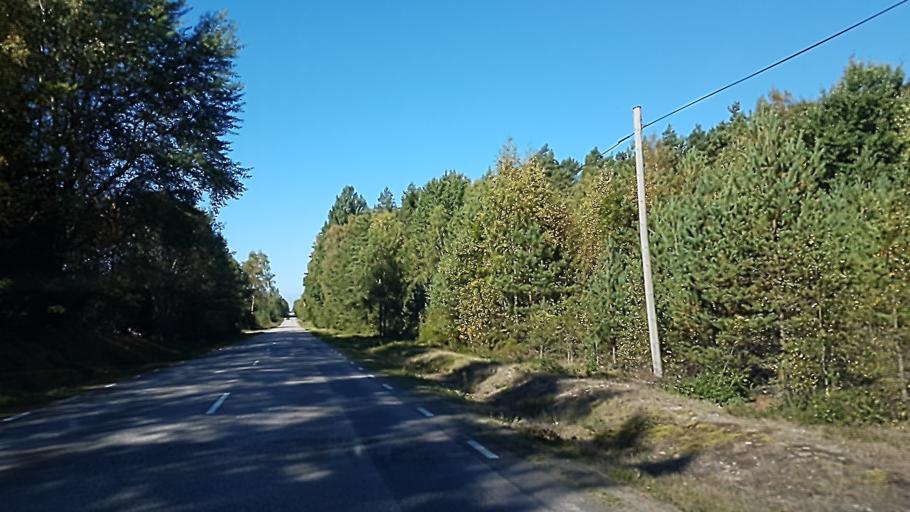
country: SE
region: Kronoberg
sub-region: Ljungby Kommun
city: Ljungby
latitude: 56.8258
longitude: 14.0485
